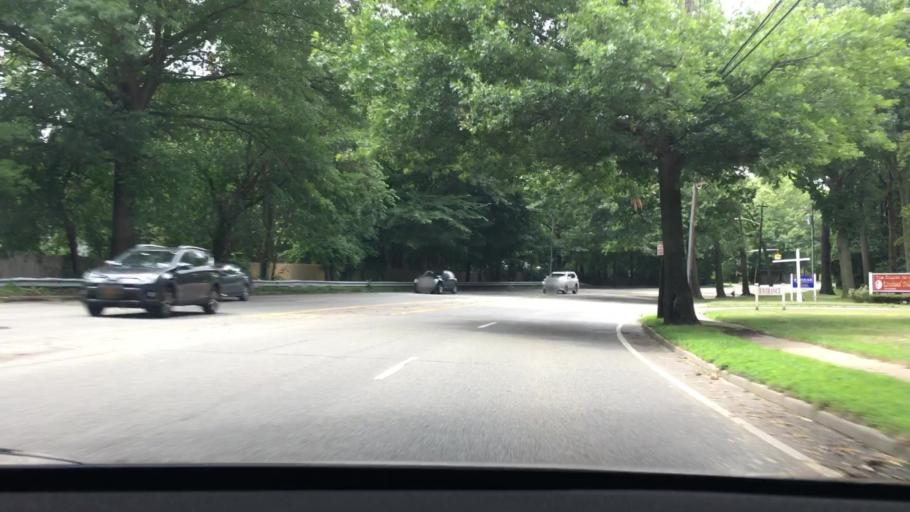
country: US
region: New York
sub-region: Nassau County
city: Woodbury
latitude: 40.8100
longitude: -73.4705
